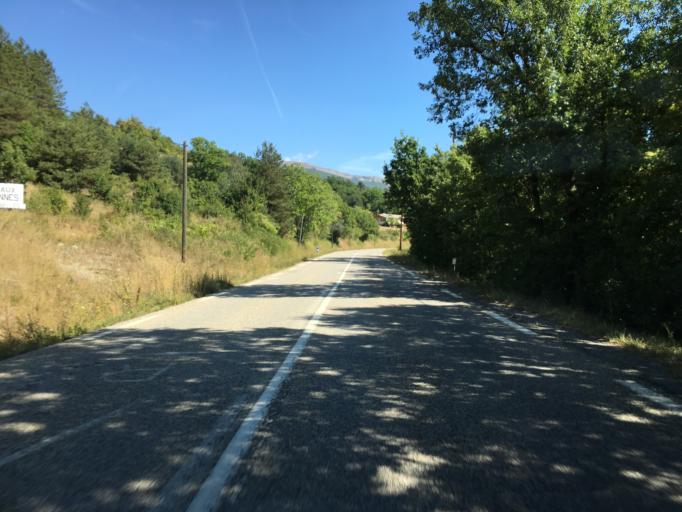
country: FR
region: Provence-Alpes-Cote d'Azur
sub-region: Departement des Hautes-Alpes
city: Serres
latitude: 44.4987
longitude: 5.7303
